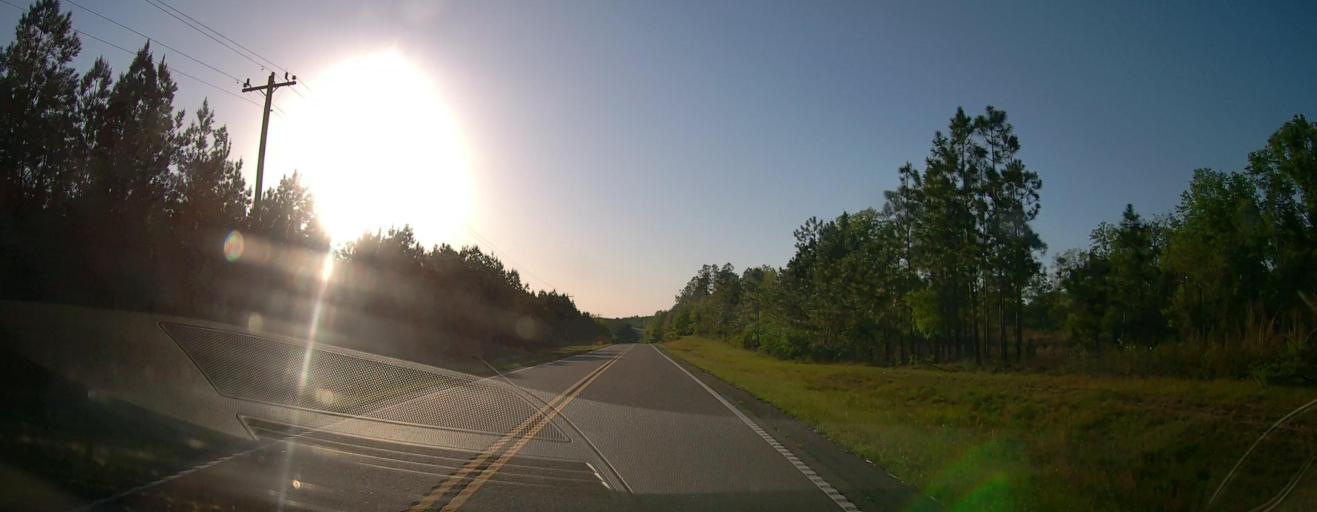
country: US
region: Georgia
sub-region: Schley County
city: Ellaville
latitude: 32.3240
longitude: -84.3216
